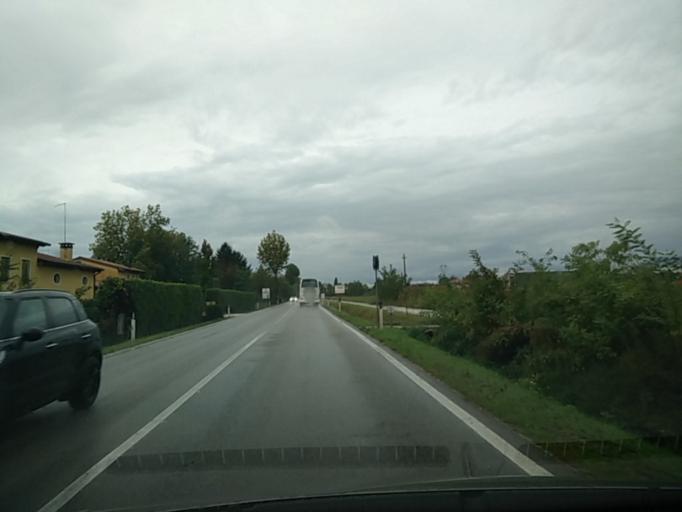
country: IT
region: Veneto
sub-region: Provincia di Treviso
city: Ramon
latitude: 45.6935
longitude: 11.8535
